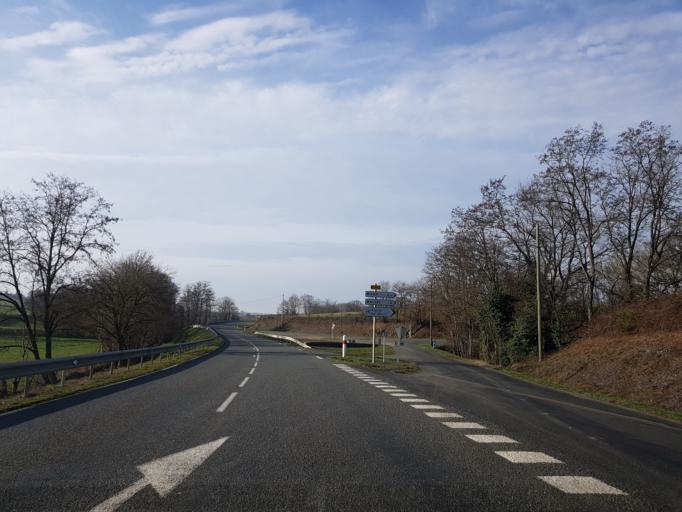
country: FR
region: Bourgogne
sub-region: Departement de Saone-et-Loire
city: Bourbon-Lancy
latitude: 46.6072
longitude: 3.8268
